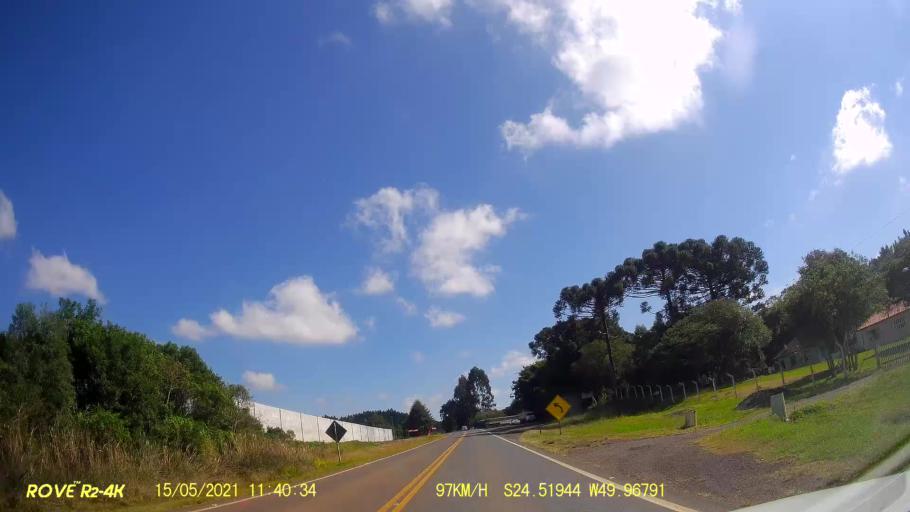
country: BR
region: Parana
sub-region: Pirai Do Sul
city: Pirai do Sul
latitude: -24.5195
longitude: -49.9679
